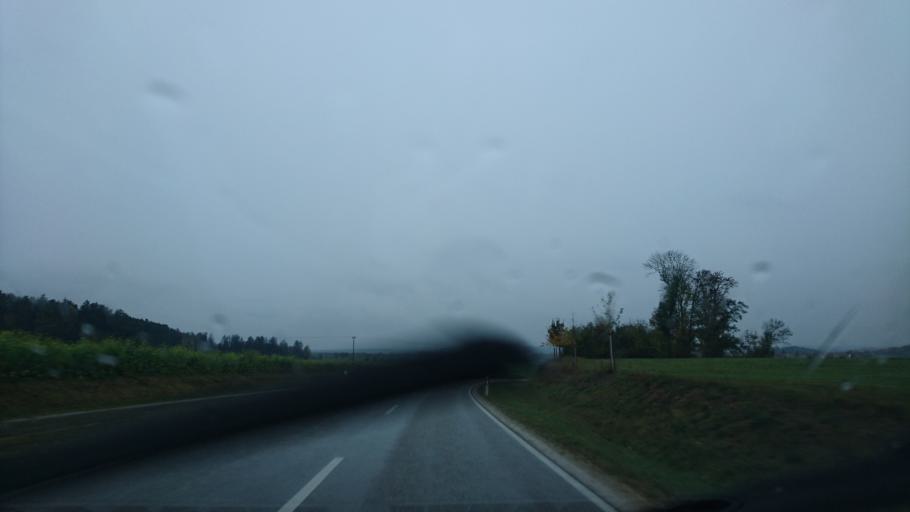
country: DE
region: Bavaria
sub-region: Swabia
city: Aichach
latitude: 48.4543
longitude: 11.1679
